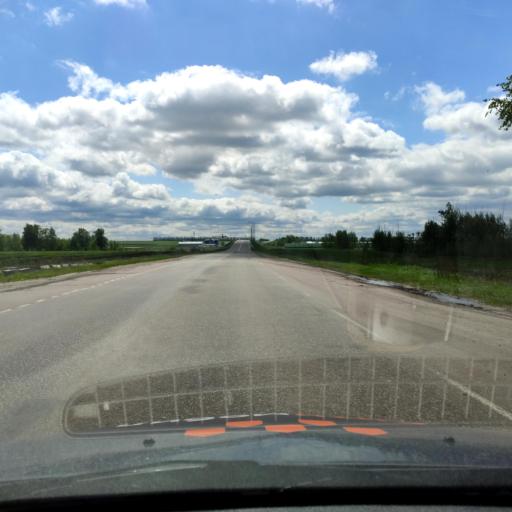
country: RU
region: Voronezj
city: Novaya Usman'
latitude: 51.6074
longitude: 39.3378
